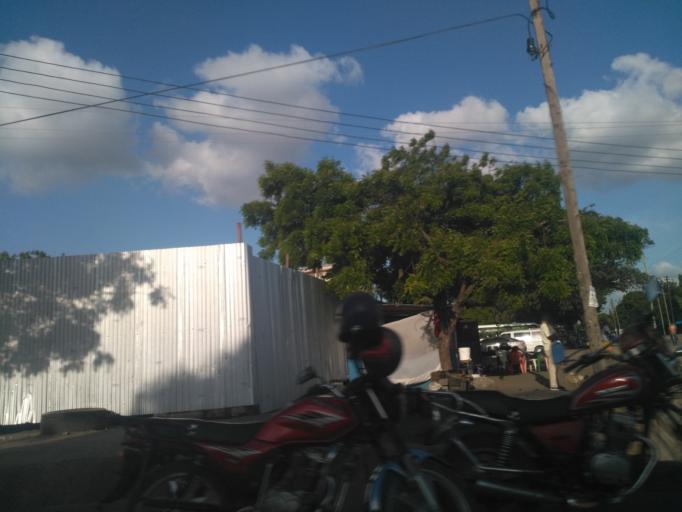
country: TZ
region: Dar es Salaam
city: Dar es Salaam
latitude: -6.8571
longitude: 39.2611
